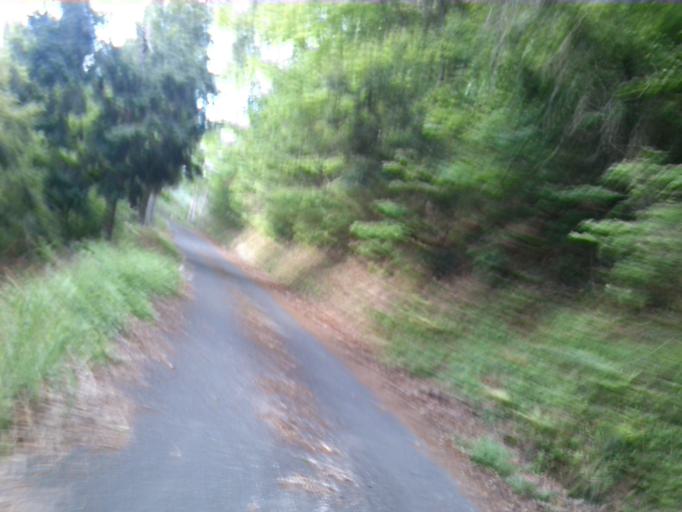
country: JP
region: Kyoto
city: Miyazu
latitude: 35.6633
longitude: 135.1320
